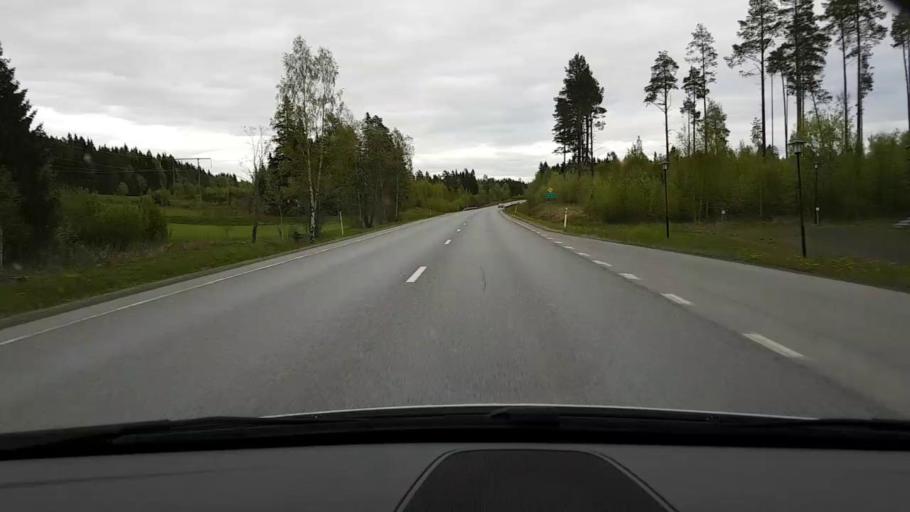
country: SE
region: Jaemtland
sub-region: Krokoms Kommun
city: Valla
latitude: 63.3348
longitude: 14.0182
